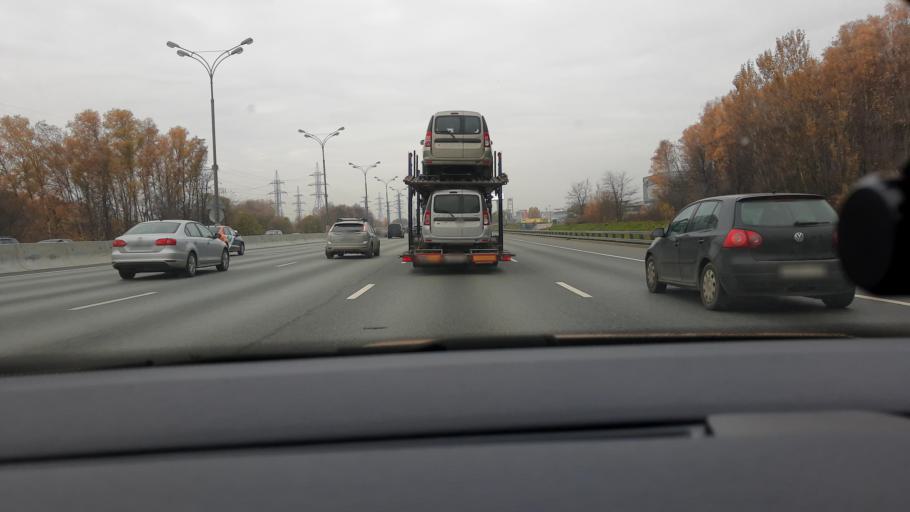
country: RU
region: Moscow
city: Lianozovo
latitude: 55.9063
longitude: 37.6042
